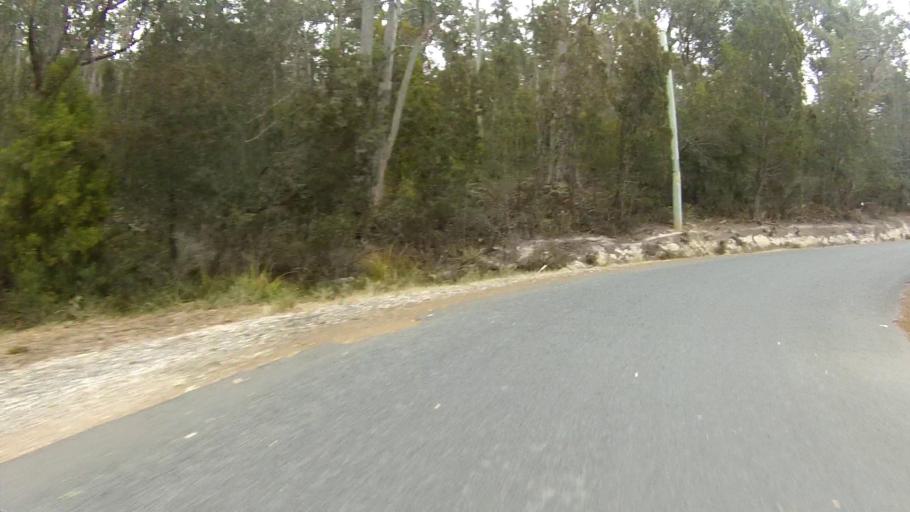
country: AU
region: Tasmania
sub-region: Huon Valley
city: Cygnet
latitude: -43.2162
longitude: 147.1040
